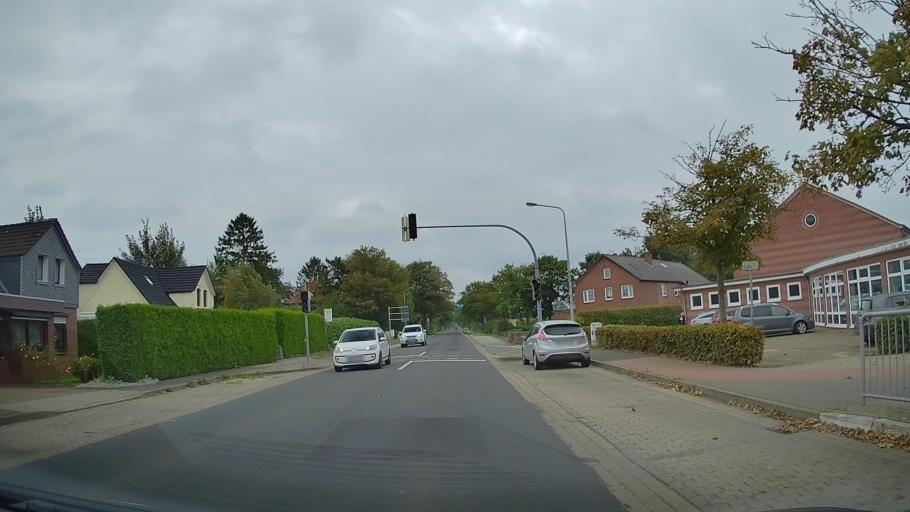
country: DE
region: Lower Saxony
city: Freiburg
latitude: 53.8215
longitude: 9.2907
